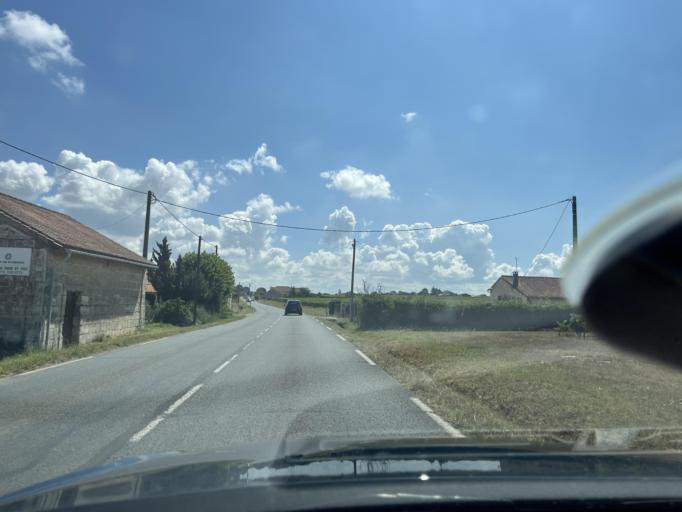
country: FR
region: Aquitaine
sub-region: Departement de la Gironde
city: Bourg
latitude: 45.0533
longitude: -0.5954
